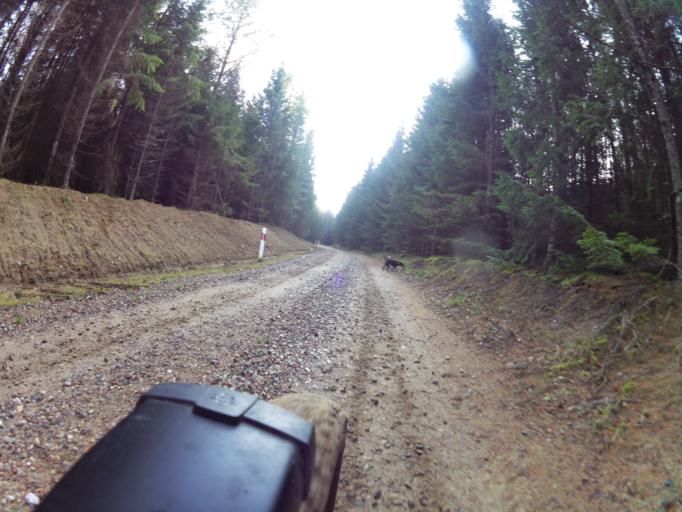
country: PL
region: West Pomeranian Voivodeship
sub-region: Powiat koszalinski
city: Polanow
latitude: 54.1782
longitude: 16.7216
